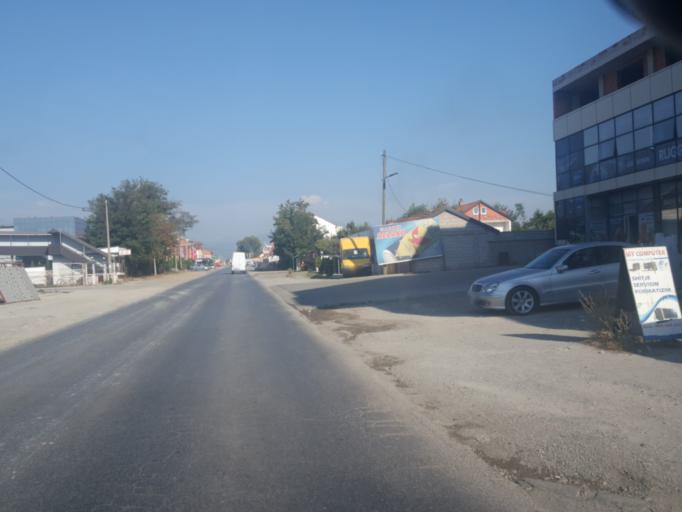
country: XK
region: Gjakova
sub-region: Komuna e Gjakoves
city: Gjakove
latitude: 42.4041
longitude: 20.4113
